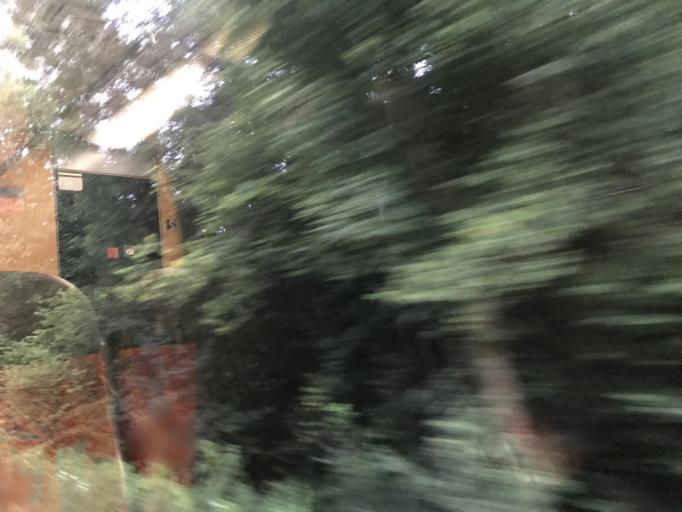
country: DE
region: Rheinland-Pfalz
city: Brachbach
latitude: 50.8217
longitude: 7.9240
